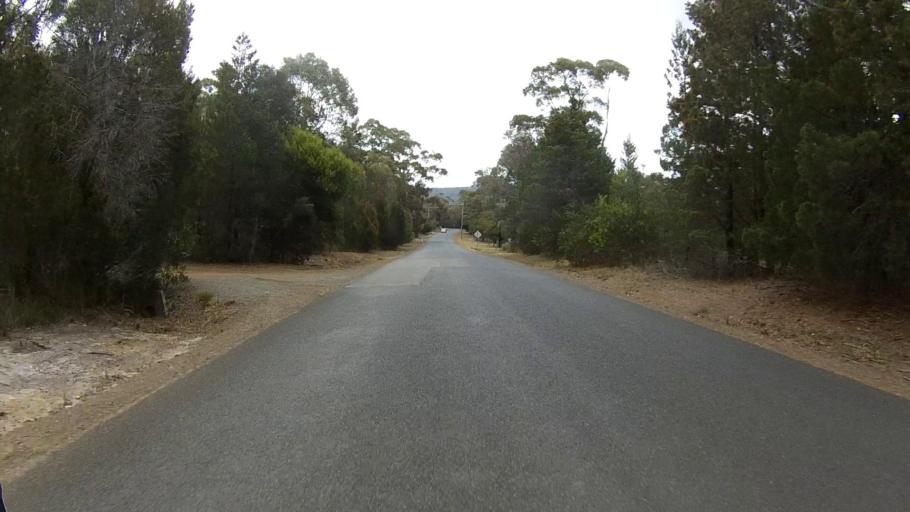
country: AU
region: Tasmania
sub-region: Sorell
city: Sorell
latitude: -42.5764
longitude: 147.9024
